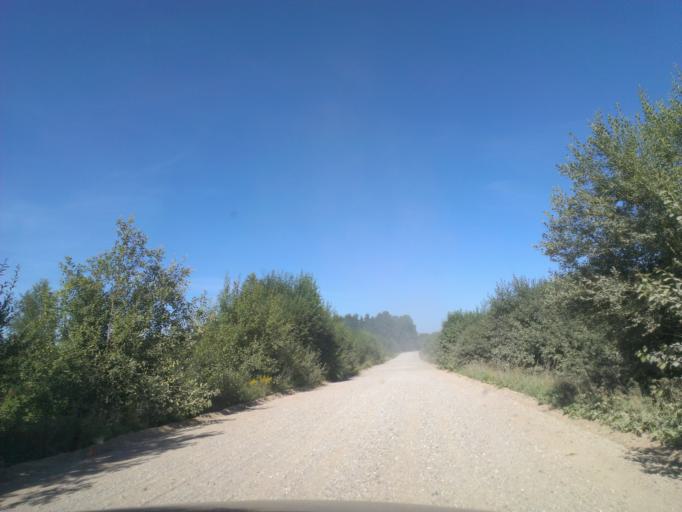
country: LV
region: Malpils
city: Malpils
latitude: 57.0505
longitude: 25.1195
